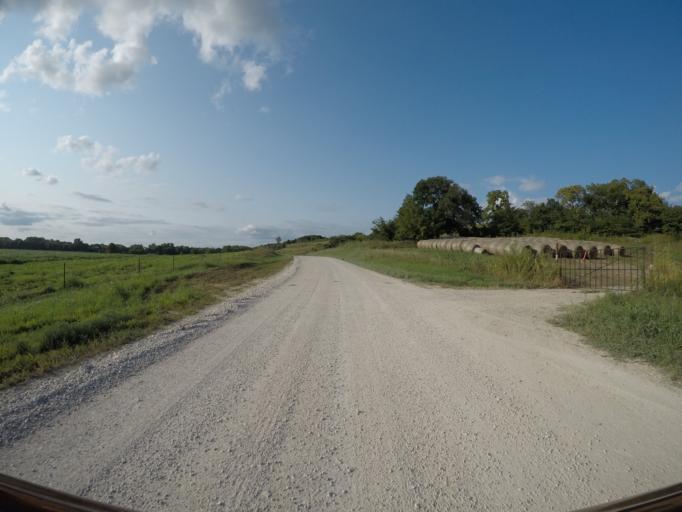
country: US
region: Kansas
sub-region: Wabaunsee County
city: Alma
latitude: 38.9035
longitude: -96.2088
